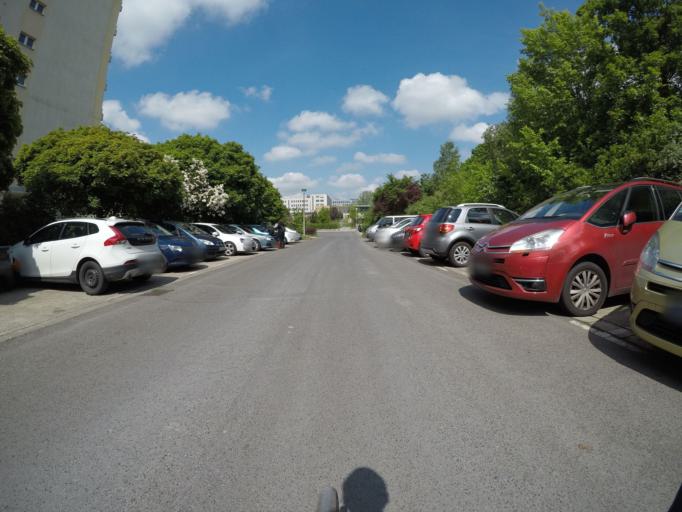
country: DE
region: Berlin
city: Hellersdorf
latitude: 52.5345
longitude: 13.6055
